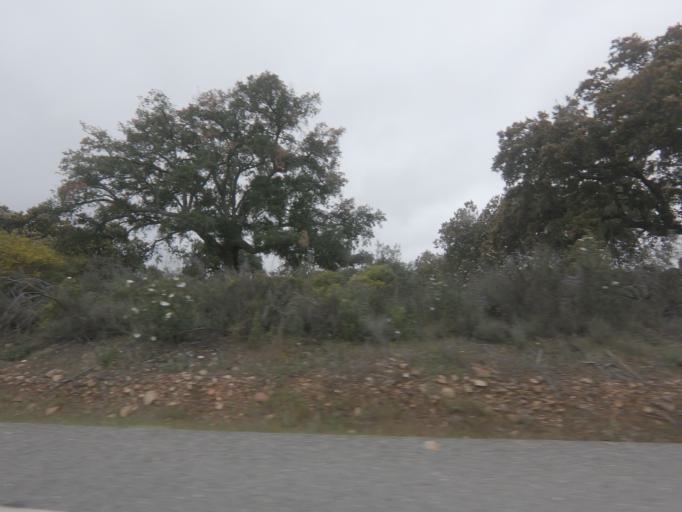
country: ES
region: Extremadura
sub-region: Provincia de Caceres
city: Malpartida de Caceres
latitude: 39.2917
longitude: -6.5221
